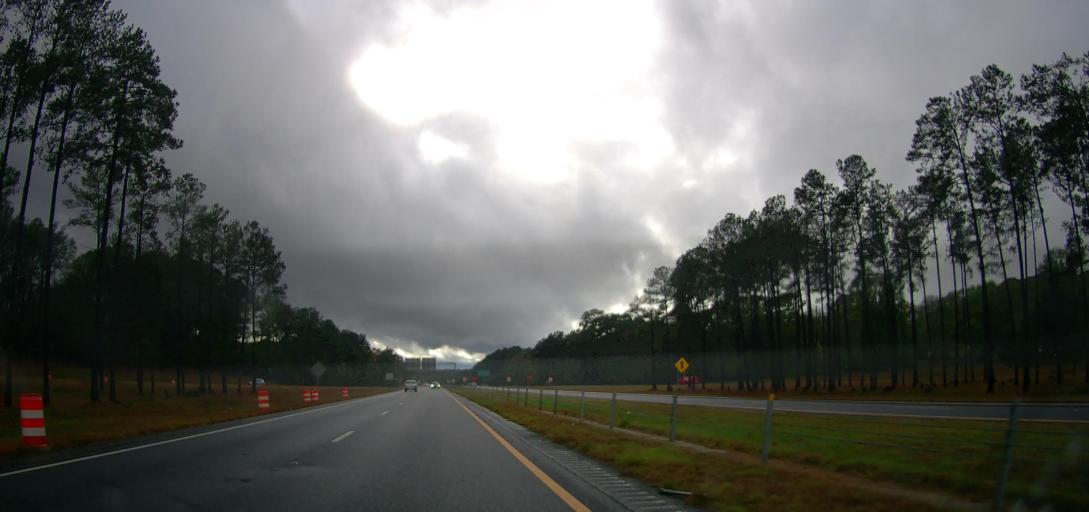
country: US
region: Georgia
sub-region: Clarke County
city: Athens
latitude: 33.9452
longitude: -83.3581
